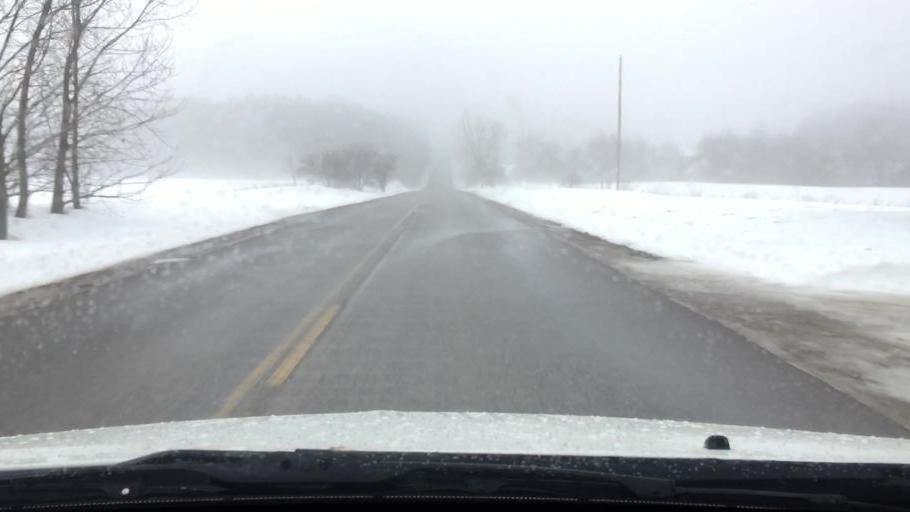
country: US
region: Michigan
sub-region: Charlevoix County
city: East Jordan
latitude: 45.1300
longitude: -85.1802
